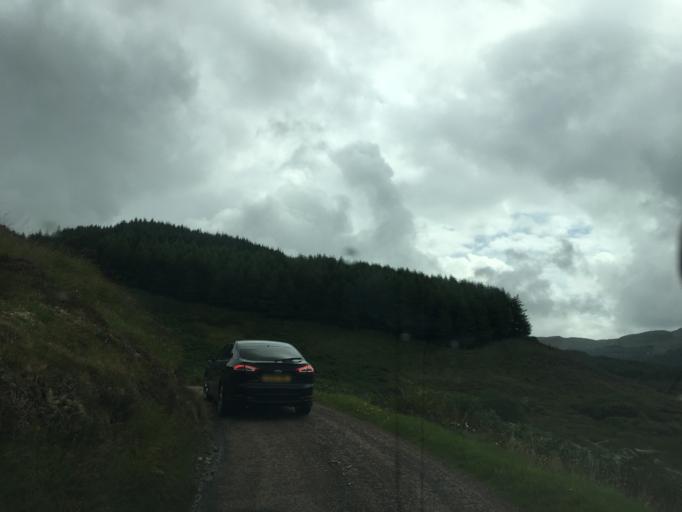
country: GB
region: Scotland
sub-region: Argyll and Bute
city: Oban
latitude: 56.2535
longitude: -5.4440
